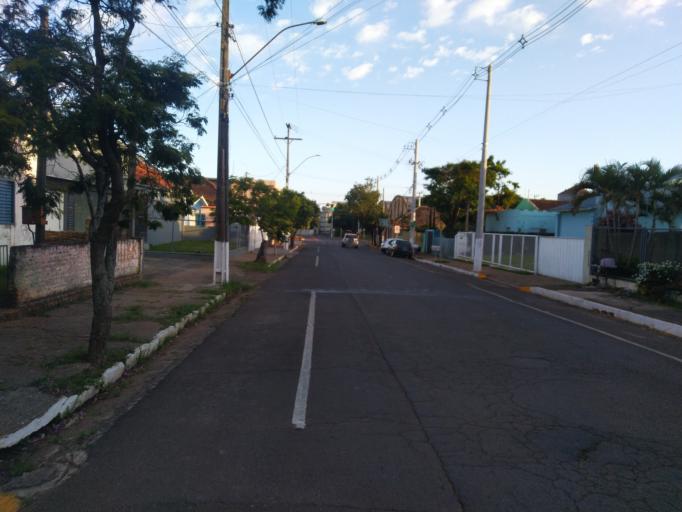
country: BR
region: Rio Grande do Sul
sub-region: Sao Borja
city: Sao Borja
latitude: -28.6507
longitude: -56.0070
